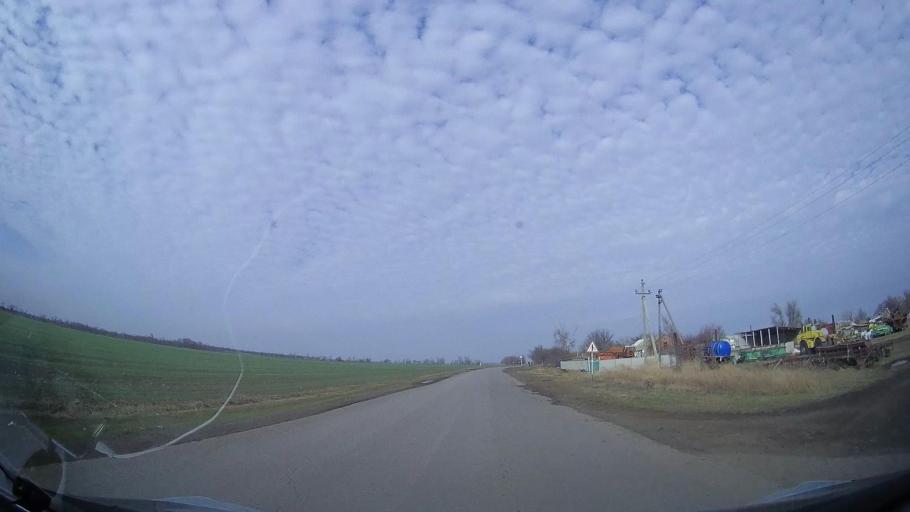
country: RU
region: Rostov
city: Gigant
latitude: 46.9231
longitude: 41.2479
